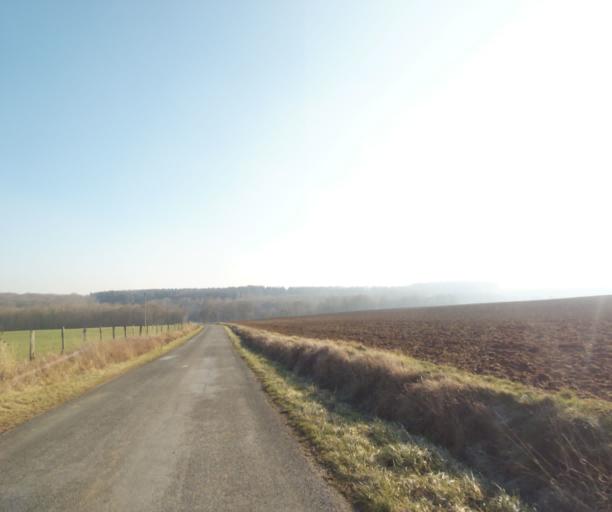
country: FR
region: Champagne-Ardenne
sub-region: Departement de la Haute-Marne
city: Bienville
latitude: 48.5021
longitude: 5.0418
